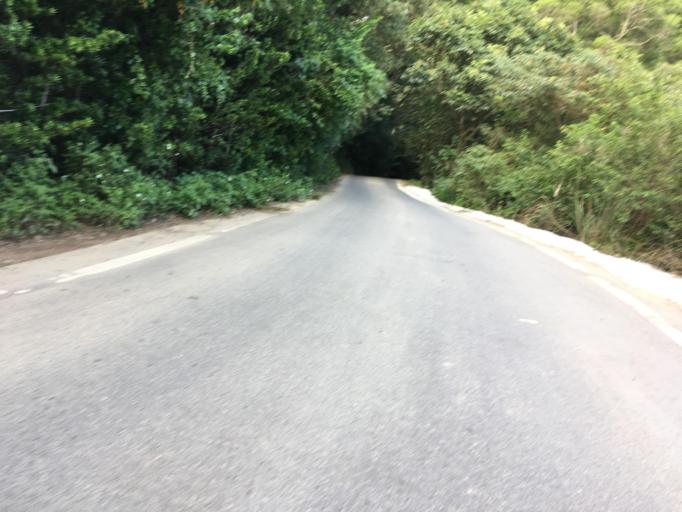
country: TW
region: Taiwan
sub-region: Yilan
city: Yilan
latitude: 24.8416
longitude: 121.7792
